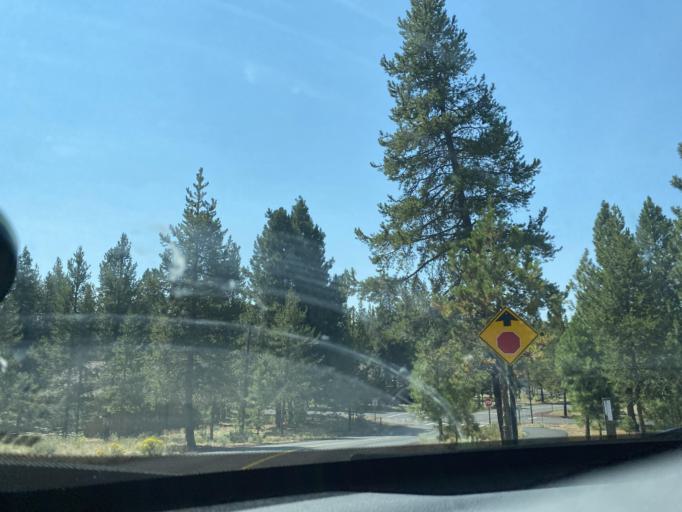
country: US
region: Oregon
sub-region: Deschutes County
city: Sunriver
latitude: 43.8933
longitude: -121.4186
